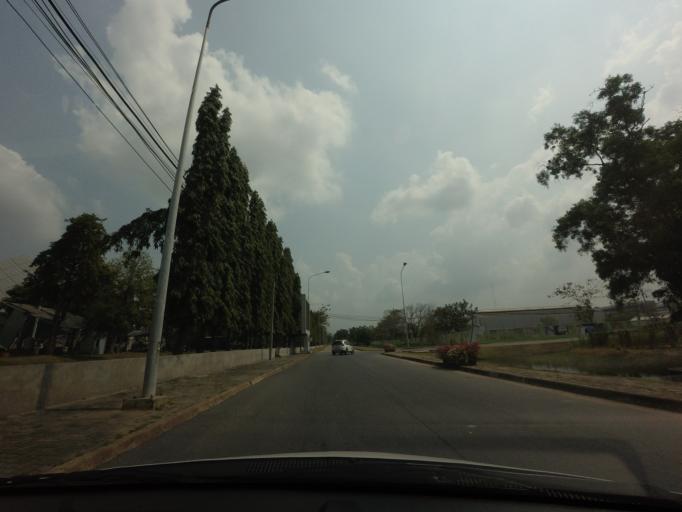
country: TH
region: Pathum Thani
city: Thanyaburi
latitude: 14.0474
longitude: 100.7159
